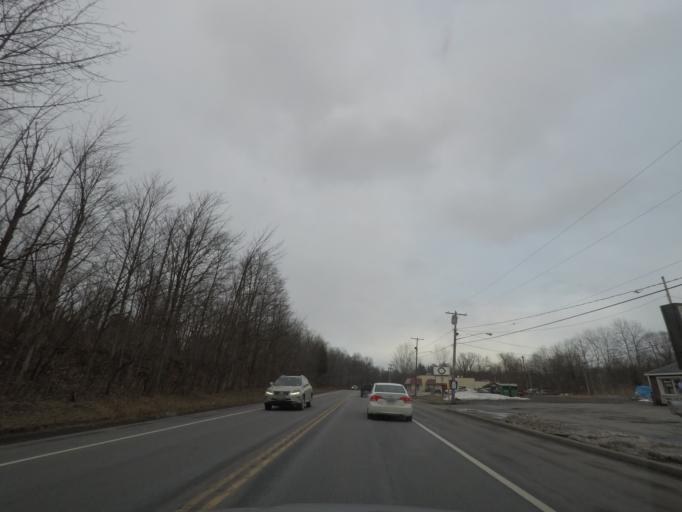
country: US
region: New York
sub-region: Oneida County
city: Sherrill
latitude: 43.0772
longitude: -75.6127
